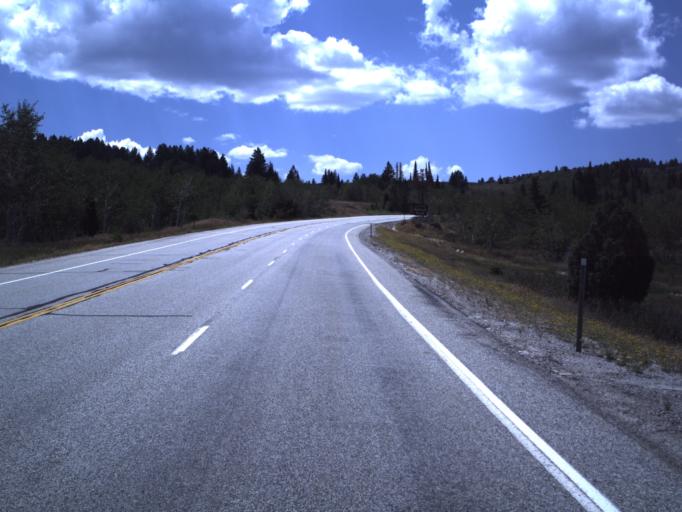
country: US
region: Idaho
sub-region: Bear Lake County
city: Paris
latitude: 41.9304
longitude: -111.4393
